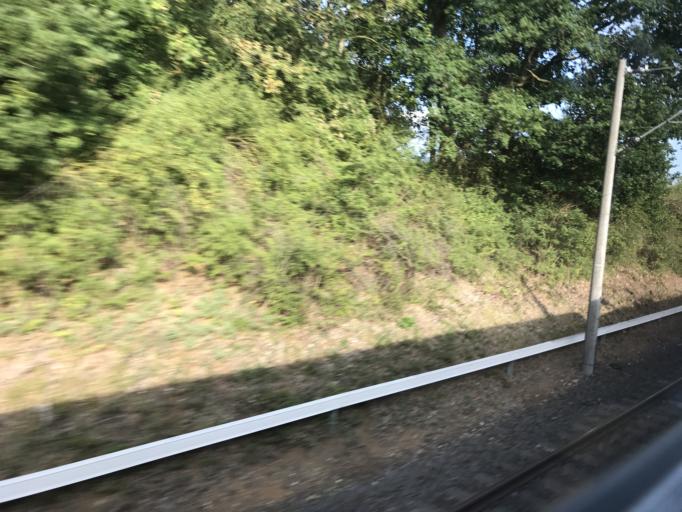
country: DE
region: Hesse
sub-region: Regierungsbezirk Giessen
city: Villmar
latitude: 50.3435
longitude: 8.2104
